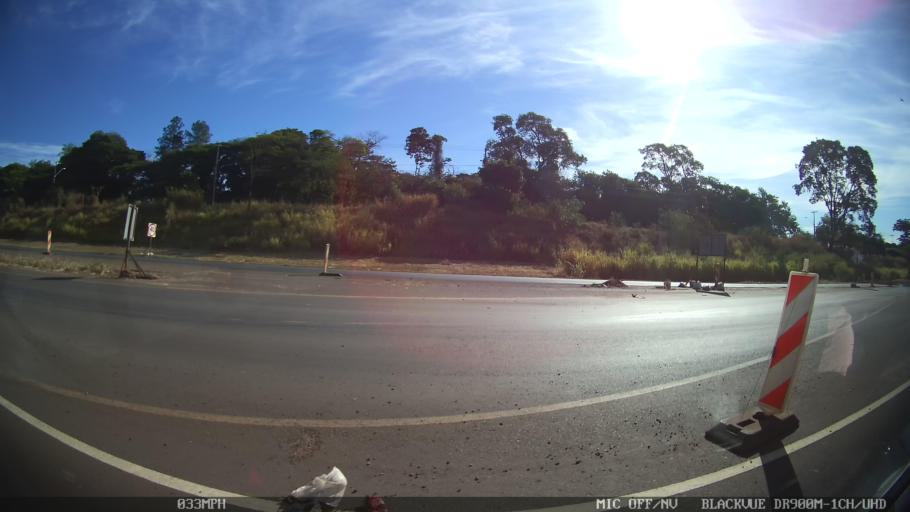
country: BR
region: Sao Paulo
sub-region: Sao Jose Do Rio Preto
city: Sao Jose do Rio Preto
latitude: -20.7794
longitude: -49.3528
